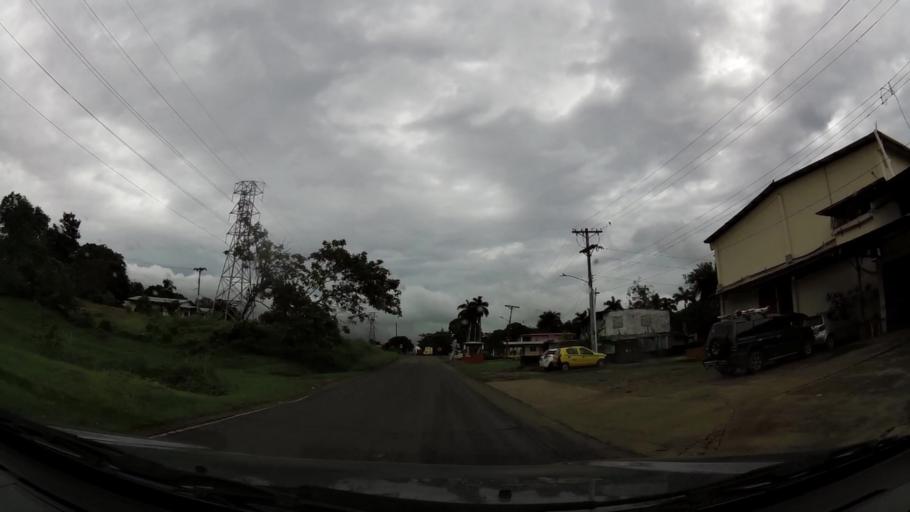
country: PA
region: Panama
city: Chilibre
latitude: 9.1486
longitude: -79.6182
